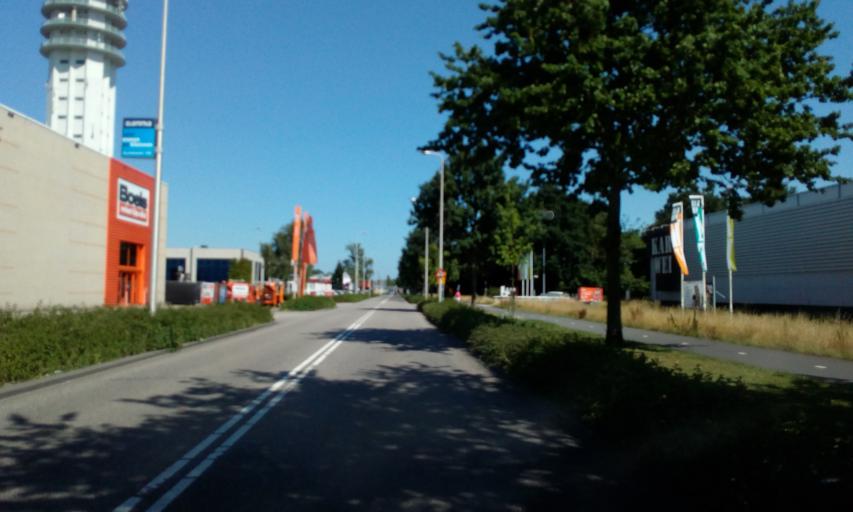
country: NL
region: South Holland
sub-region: Gemeente Alphen aan den Rijn
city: Alphen aan den Rijn
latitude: 52.1359
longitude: 4.6484
